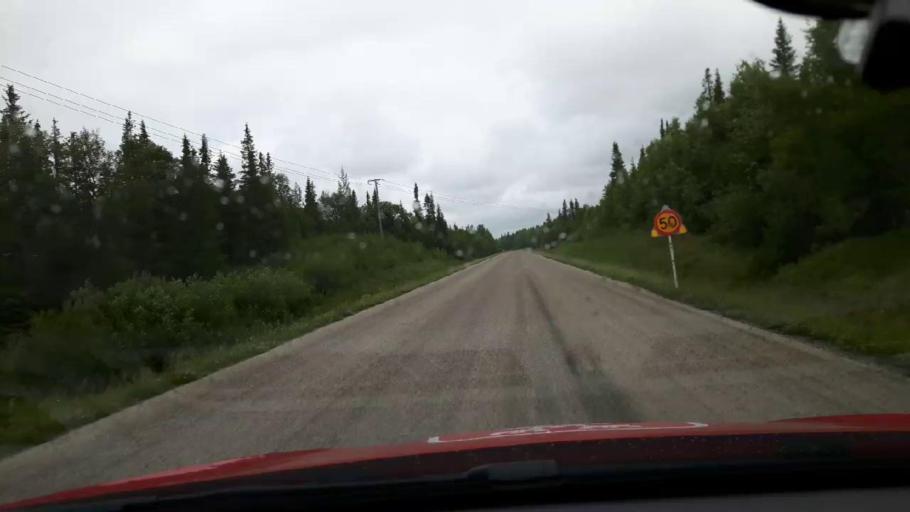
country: SE
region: Jaemtland
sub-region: Are Kommun
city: Are
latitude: 63.2617
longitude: 12.4123
